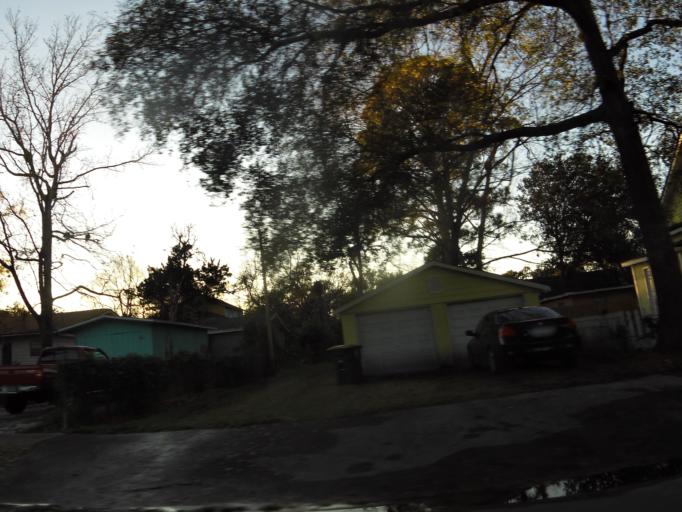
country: US
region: Florida
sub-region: Duval County
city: Jacksonville
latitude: 30.3154
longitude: -81.6954
